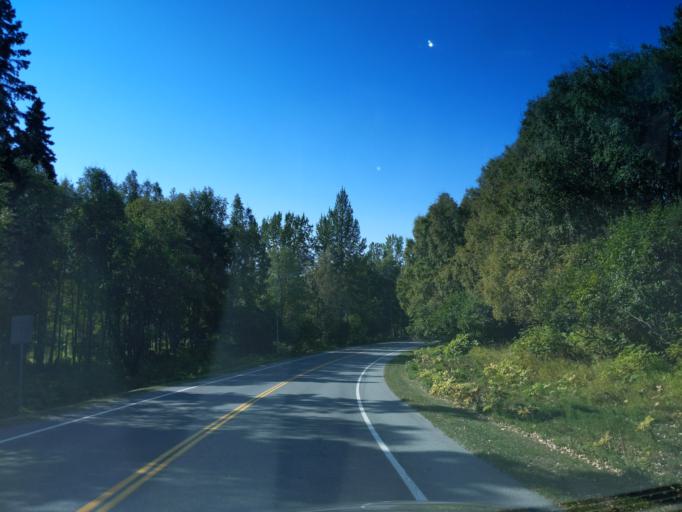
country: US
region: Alaska
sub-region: Anchorage Municipality
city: Anchorage
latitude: 61.1535
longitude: -150.0195
